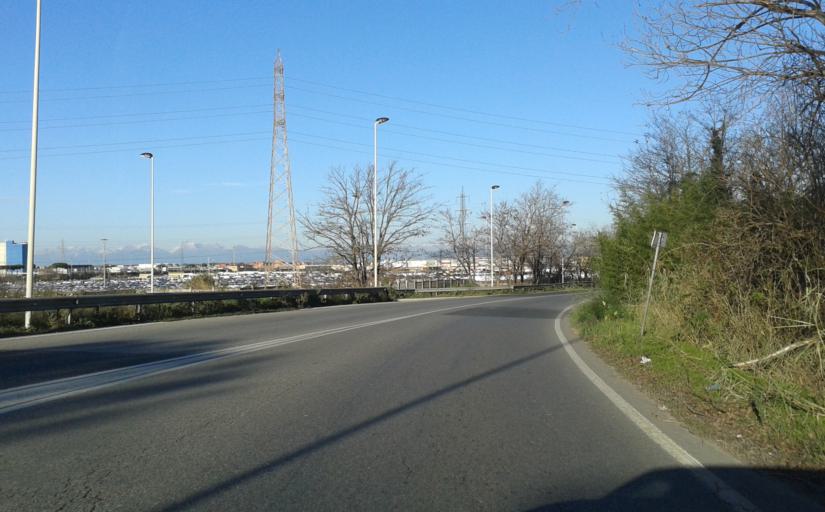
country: IT
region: Tuscany
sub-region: Provincia di Livorno
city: Livorno
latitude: 43.5701
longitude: 10.3235
